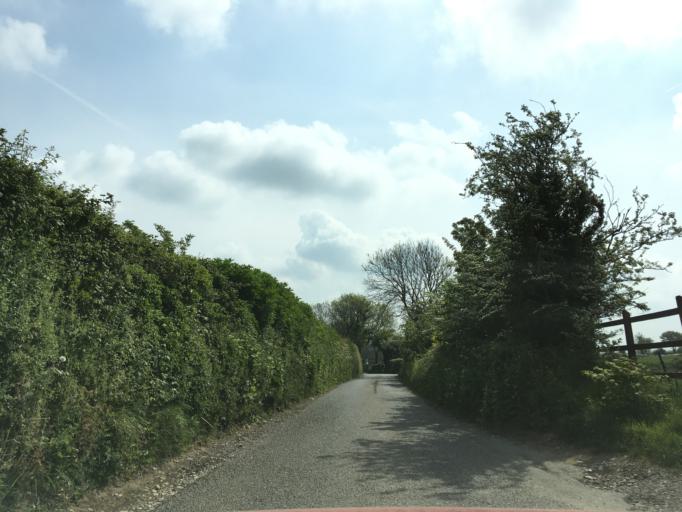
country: GB
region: England
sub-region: North Somerset
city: Dundry
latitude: 51.3972
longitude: -2.6304
